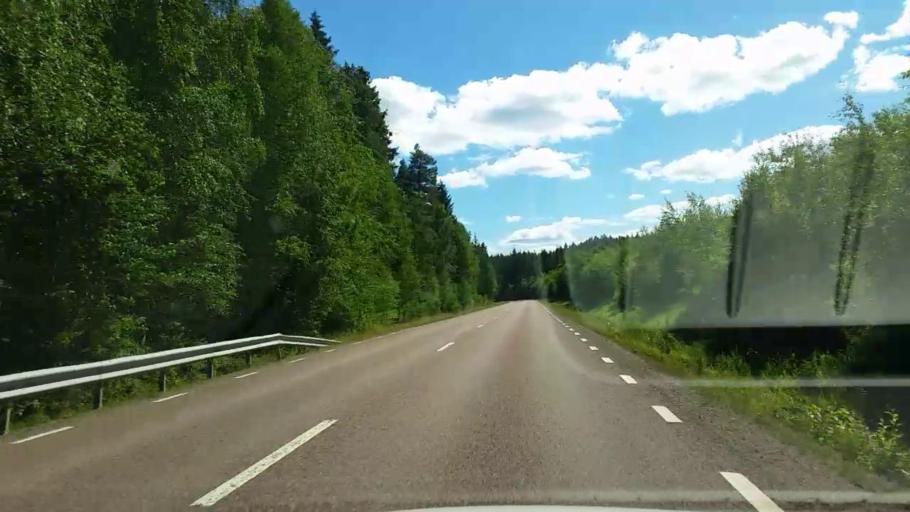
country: SE
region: Dalarna
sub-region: Faluns Kommun
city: Svardsjo
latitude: 60.9611
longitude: 15.6918
